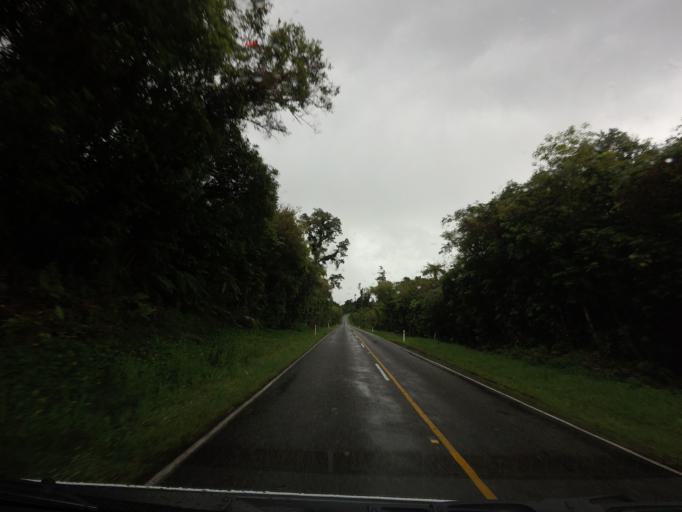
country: NZ
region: West Coast
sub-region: Westland District
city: Hokitika
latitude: -43.0625
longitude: 170.6327
